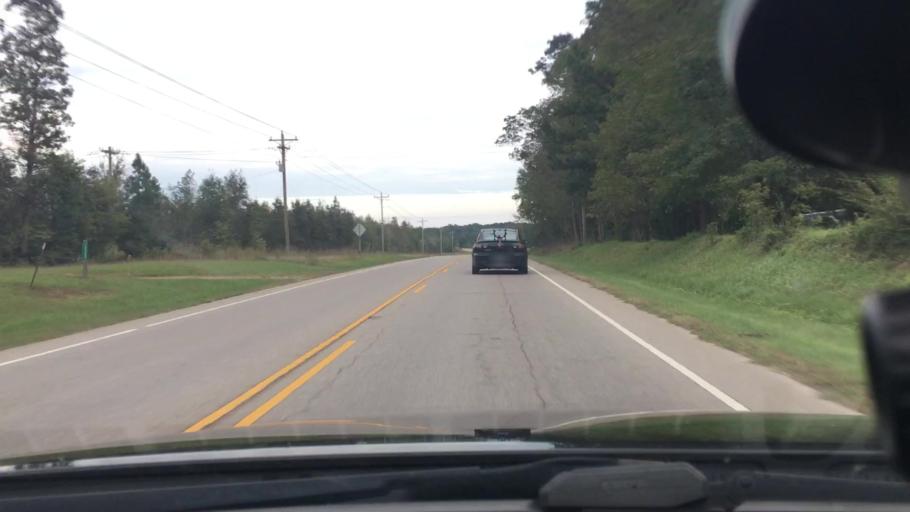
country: US
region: North Carolina
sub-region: Moore County
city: Robbins
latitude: 35.4006
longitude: -79.5531
